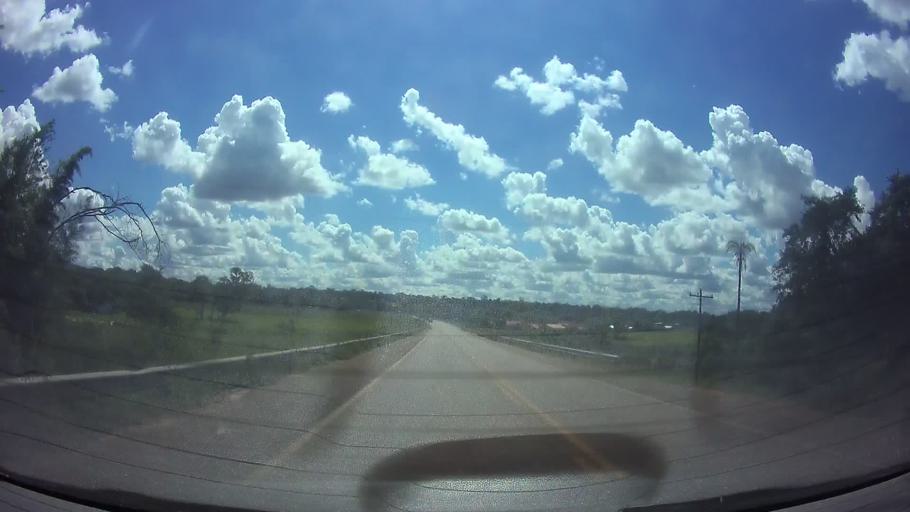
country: PY
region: Paraguari
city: La Colmena
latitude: -25.8992
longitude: -56.7865
